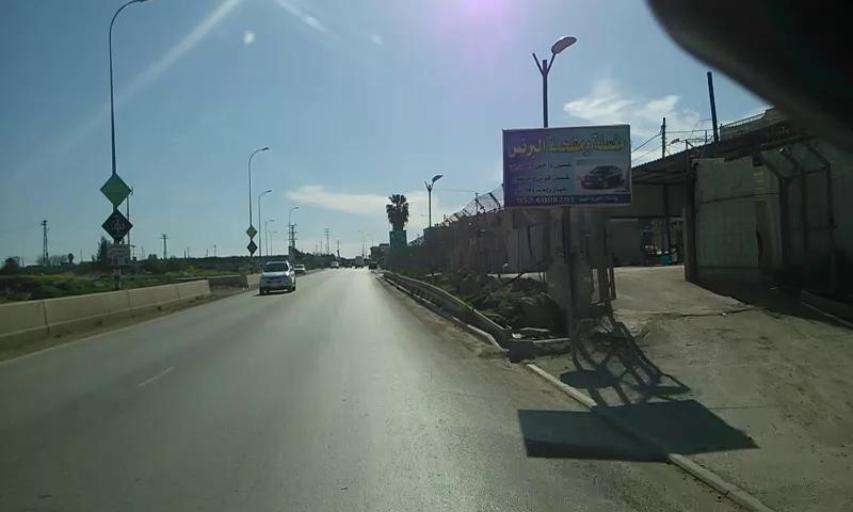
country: PS
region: West Bank
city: Ar Ram wa Dahiyat al Barid
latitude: 31.8570
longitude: 35.2385
